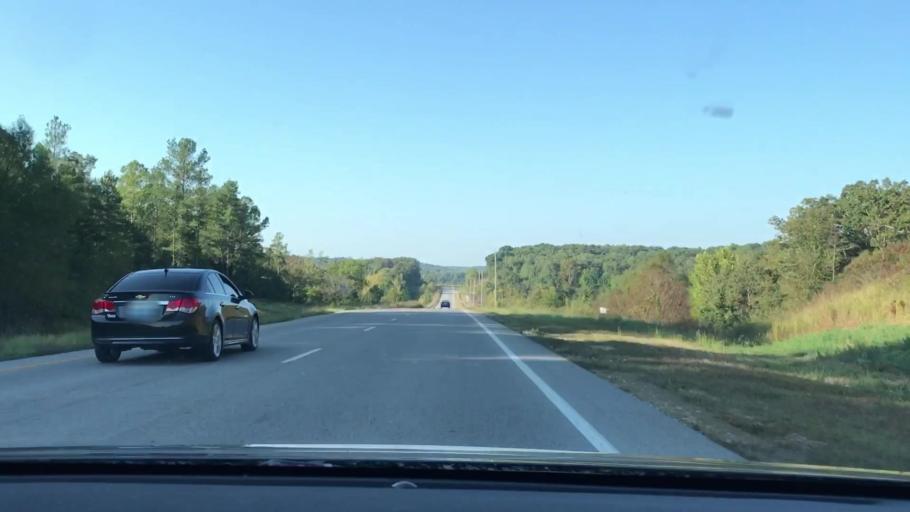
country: US
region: Kentucky
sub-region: Trigg County
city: Cadiz
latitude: 36.7993
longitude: -87.9968
